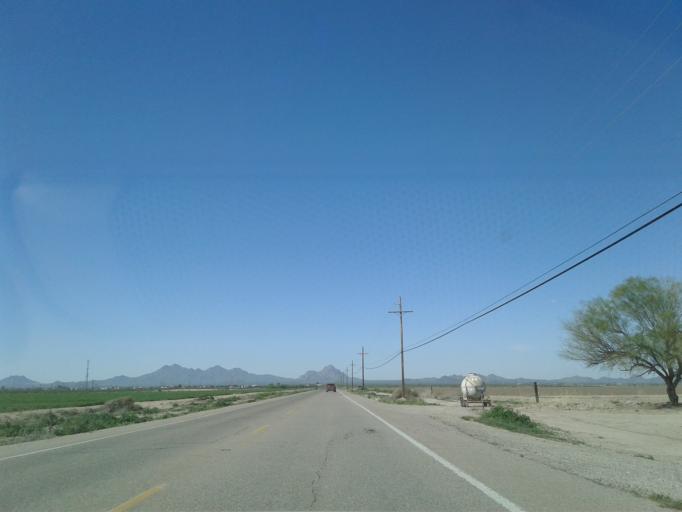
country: US
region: Arizona
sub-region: Pima County
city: Avra Valley
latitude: 32.4513
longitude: -111.2871
